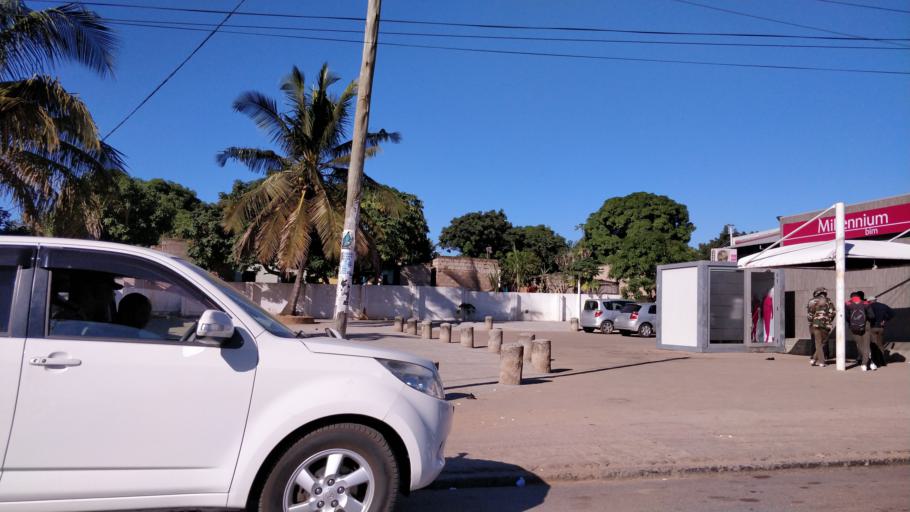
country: MZ
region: Maputo City
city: Maputo
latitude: -25.9271
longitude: 32.6044
